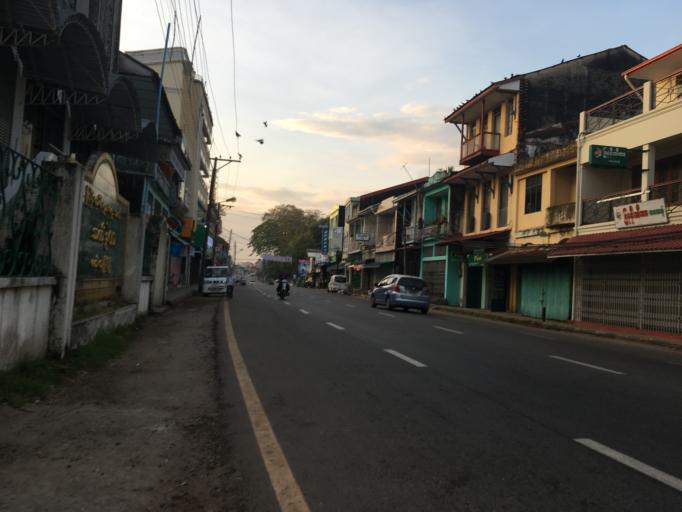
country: MM
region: Mon
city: Mawlamyine
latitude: 16.4859
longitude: 97.6192
